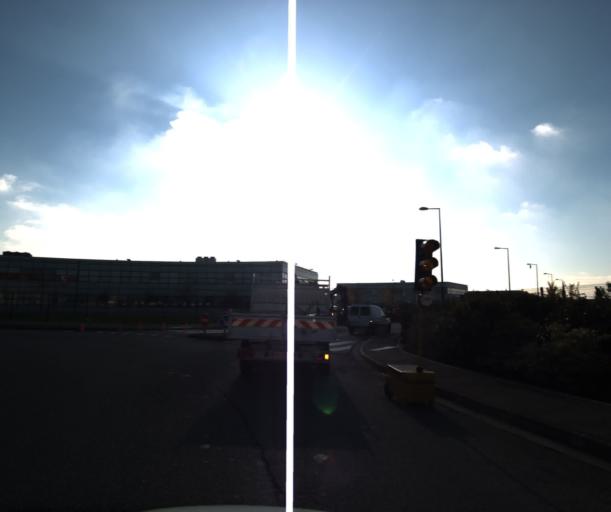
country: FR
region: Midi-Pyrenees
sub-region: Departement de la Haute-Garonne
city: Colomiers
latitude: 43.6044
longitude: 1.3608
